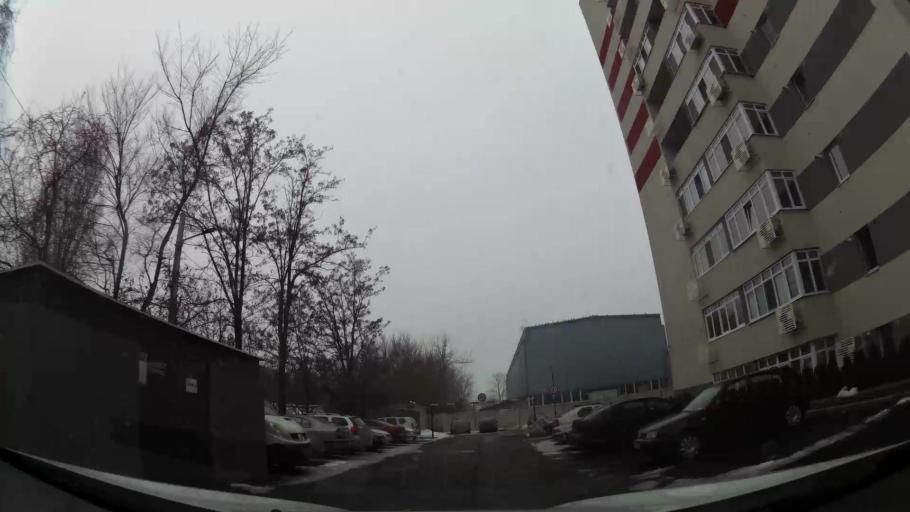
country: RO
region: Ilfov
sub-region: Comuna Chiajna
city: Rosu
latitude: 44.4357
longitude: 25.9995
